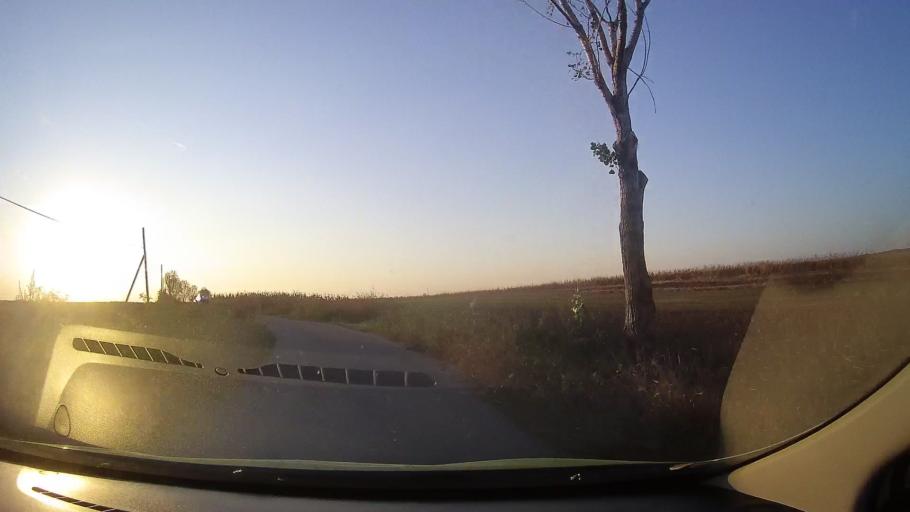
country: RO
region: Bihor
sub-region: Comuna Rosiori
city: Rosiori
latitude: 47.2559
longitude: 21.9818
